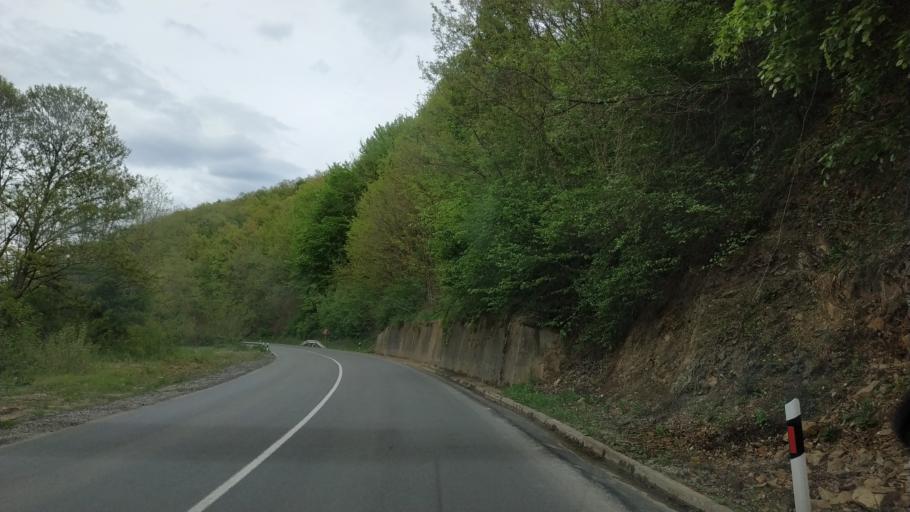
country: RS
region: Central Serbia
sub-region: Nisavski Okrug
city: Aleksinac
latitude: 43.6496
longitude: 21.7338
